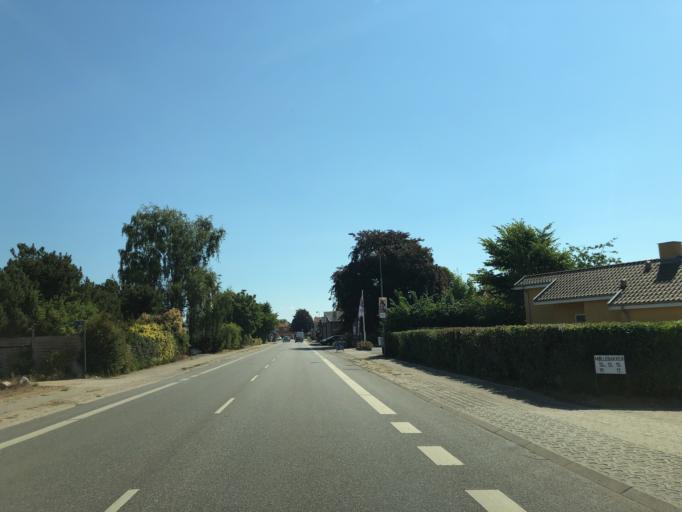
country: DK
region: Zealand
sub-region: Odsherred Kommune
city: Nykobing Sjaelland
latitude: 55.9430
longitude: 11.7477
